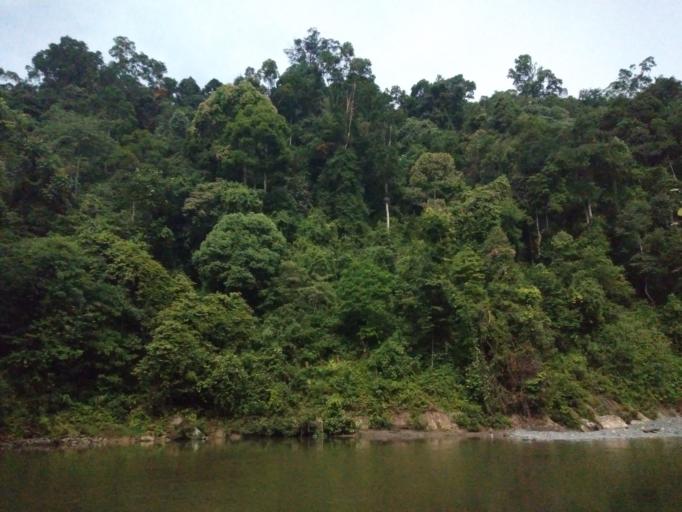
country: ID
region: Aceh
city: Tenggulun
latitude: 3.6952
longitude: 98.0695
